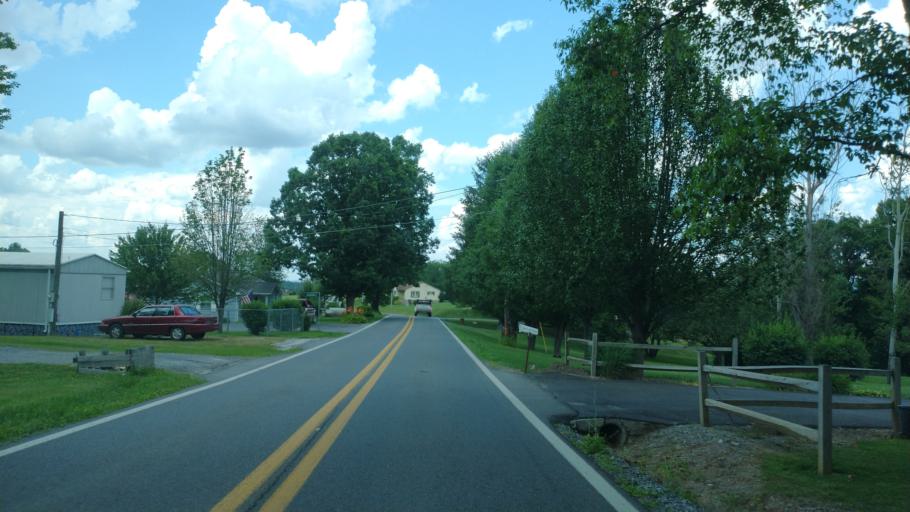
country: US
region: West Virginia
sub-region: Mercer County
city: Athens
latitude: 37.4035
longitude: -81.0596
